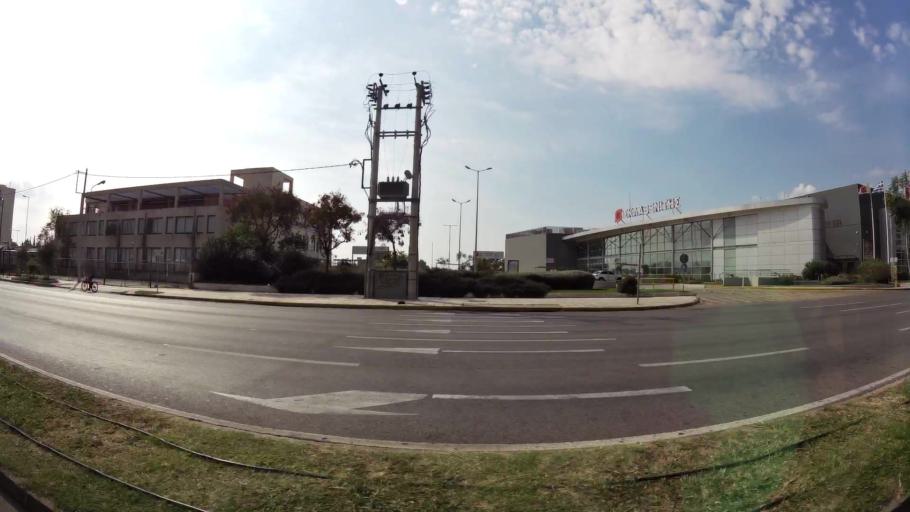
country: GR
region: Attica
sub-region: Nomarchia Athinas
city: Athens
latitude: 37.9908
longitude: 23.7025
